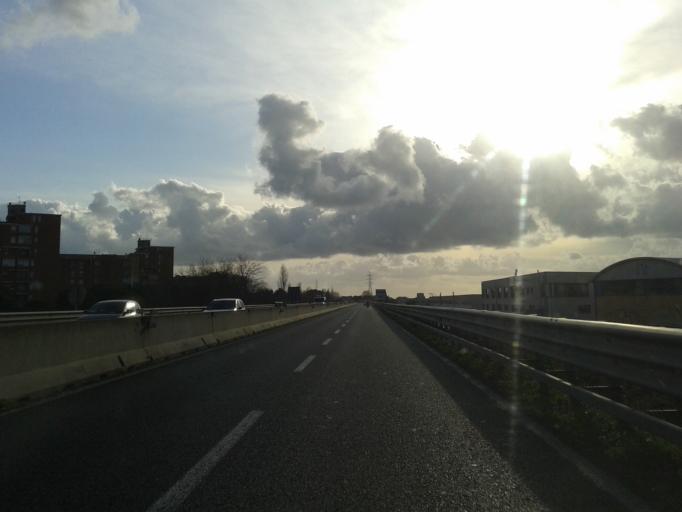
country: IT
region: Tuscany
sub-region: Provincia di Livorno
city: Livorno
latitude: 43.5409
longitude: 10.3378
